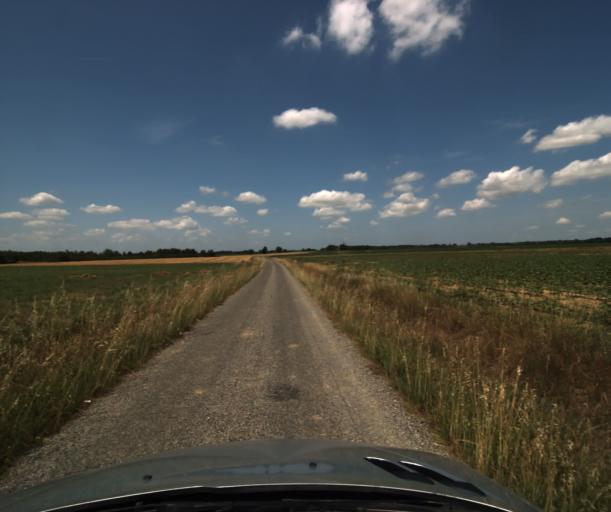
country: FR
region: Midi-Pyrenees
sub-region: Departement de la Haute-Garonne
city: Labastidette
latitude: 43.4725
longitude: 1.2035
